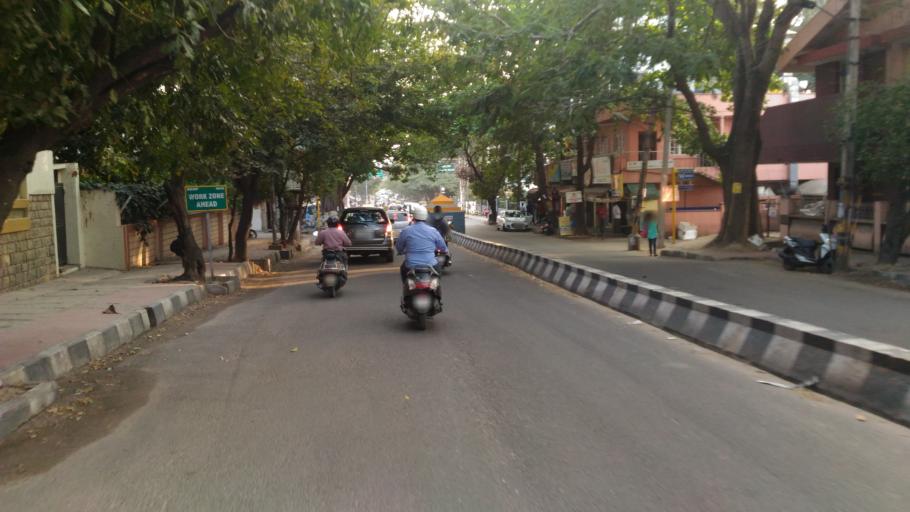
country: IN
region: Karnataka
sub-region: Bangalore Urban
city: Bangalore
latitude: 12.9073
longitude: 77.5952
